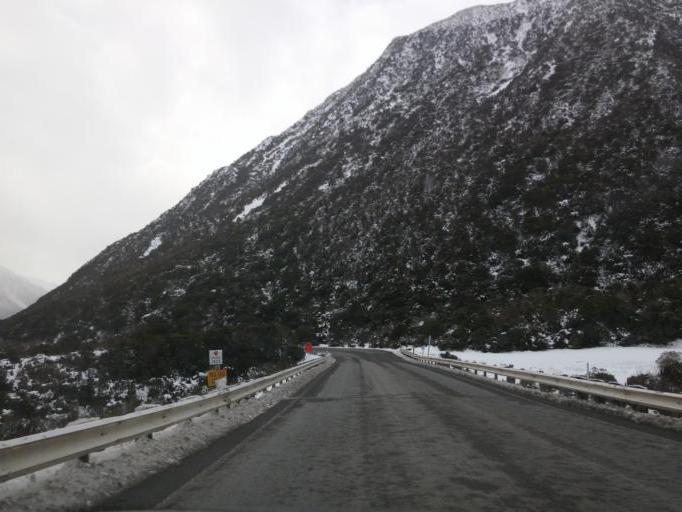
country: NZ
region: West Coast
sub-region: Grey District
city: Greymouth
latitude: -42.8953
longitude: 171.5588
